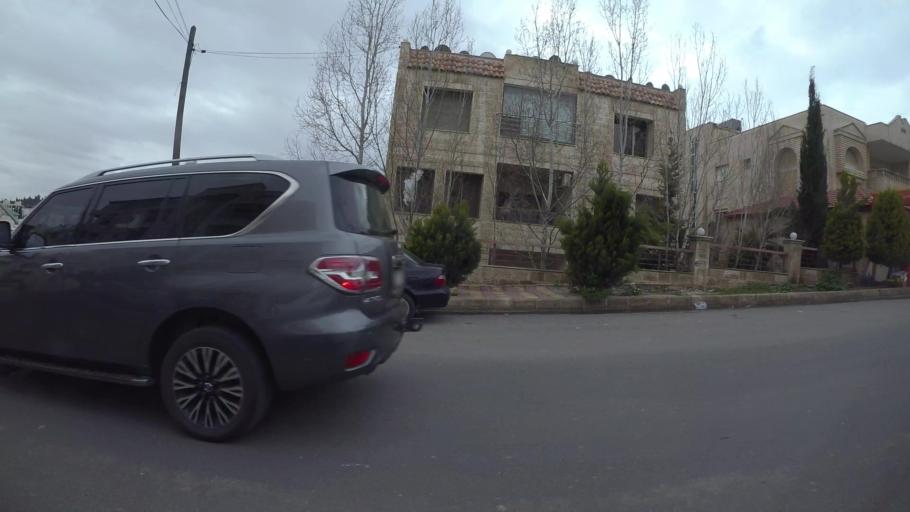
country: JO
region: Amman
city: Wadi as Sir
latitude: 31.9845
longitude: 35.8374
